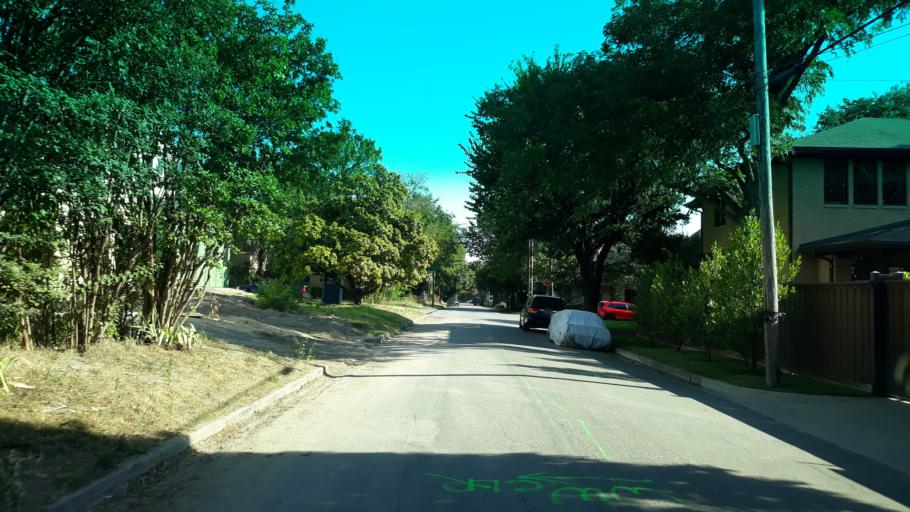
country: US
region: Texas
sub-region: Dallas County
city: Highland Park
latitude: 32.8249
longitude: -96.7581
